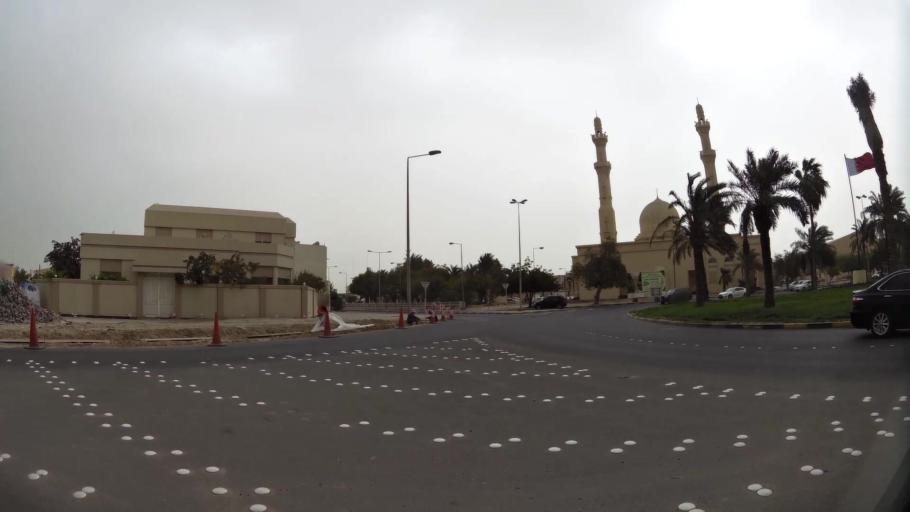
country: BH
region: Northern
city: Madinat `Isa
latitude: 26.1711
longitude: 50.5455
